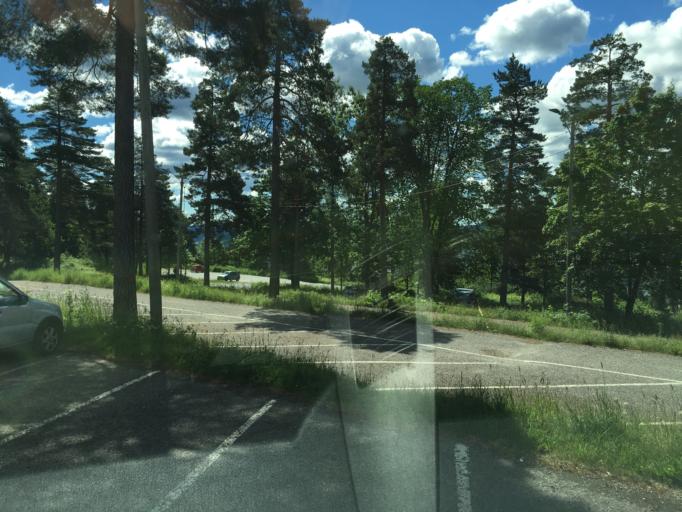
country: NO
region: Buskerud
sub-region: Drammen
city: Drammen
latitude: 59.7527
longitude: 10.2022
